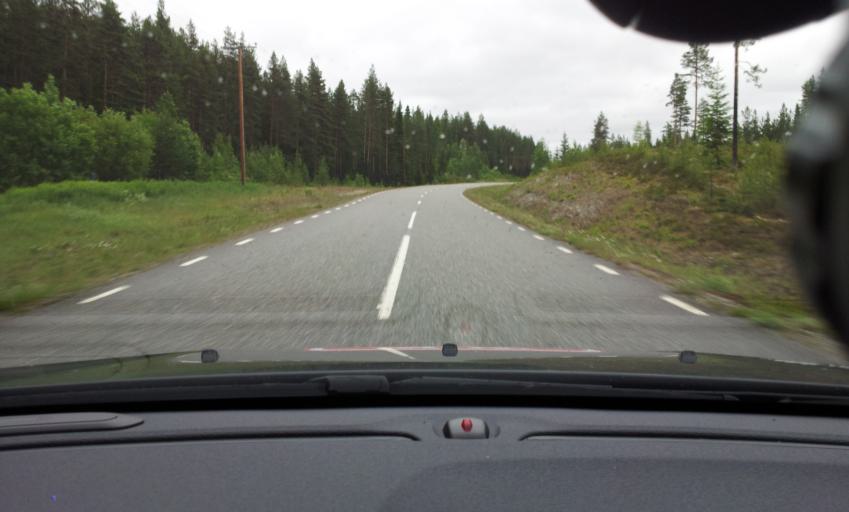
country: SE
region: Jaemtland
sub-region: Ragunda Kommun
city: Hammarstrand
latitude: 63.2798
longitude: 15.8001
